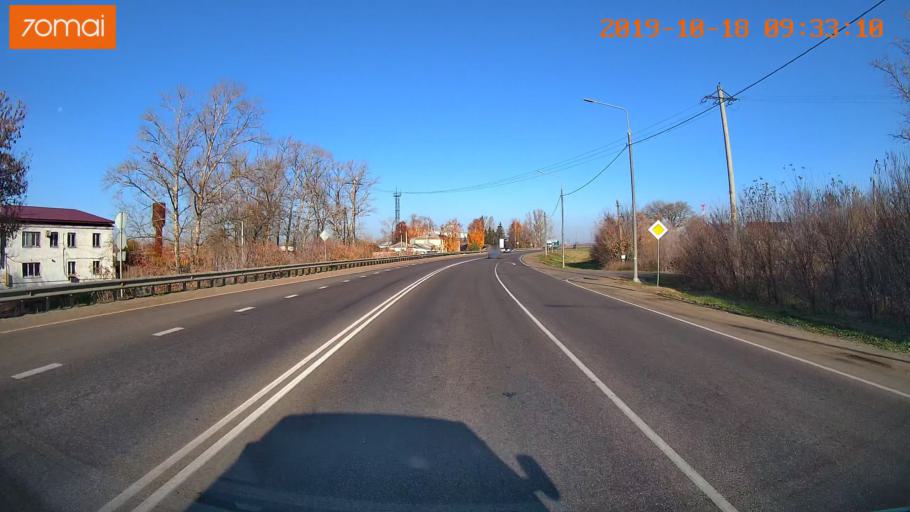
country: RU
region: Tula
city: Yefremov
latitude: 53.1639
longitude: 38.1524
